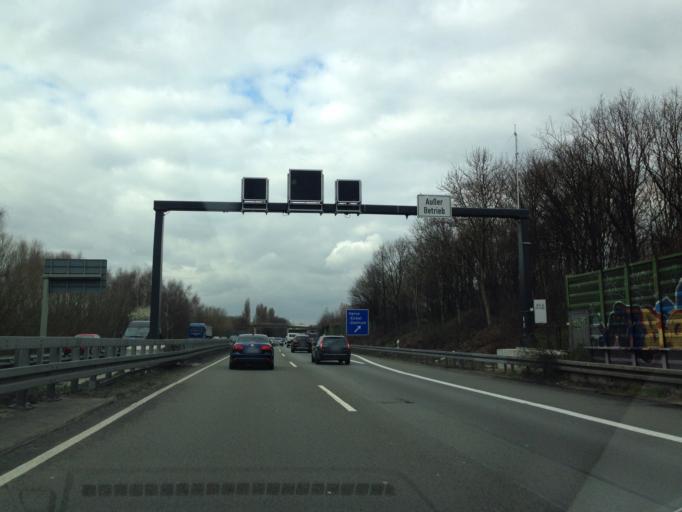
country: DE
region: North Rhine-Westphalia
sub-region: Regierungsbezirk Arnsberg
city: Herne
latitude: 51.5267
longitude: 7.2080
